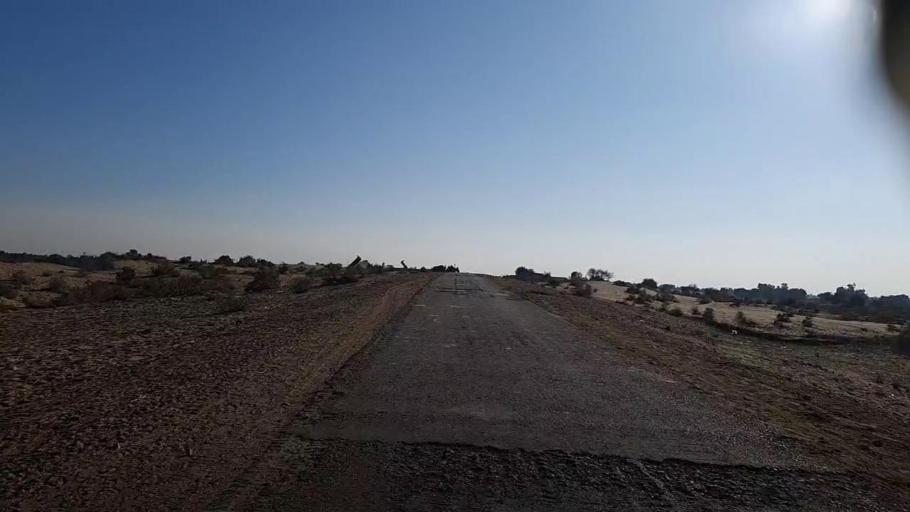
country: PK
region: Sindh
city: Khairpur
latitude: 27.9028
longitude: 69.7490
